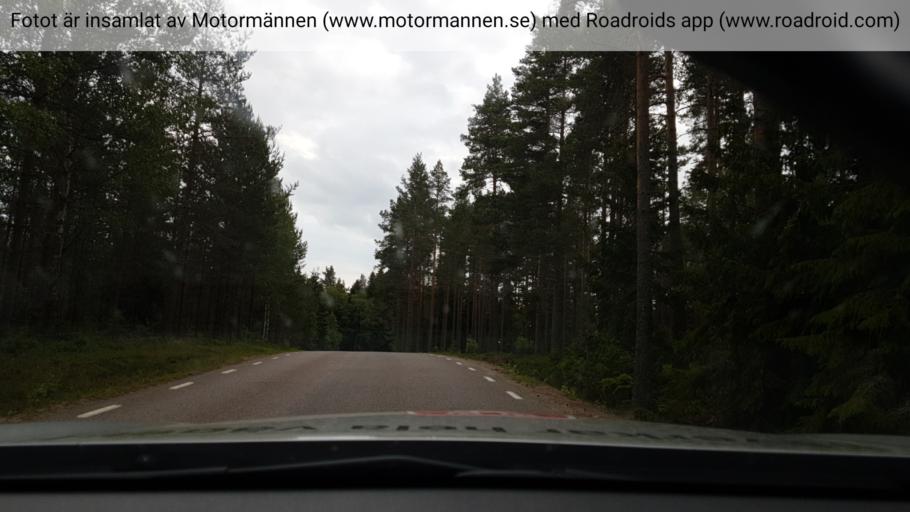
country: SE
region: Joenkoeping
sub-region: Habo Kommun
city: Habo
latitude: 58.0264
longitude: 14.0150
